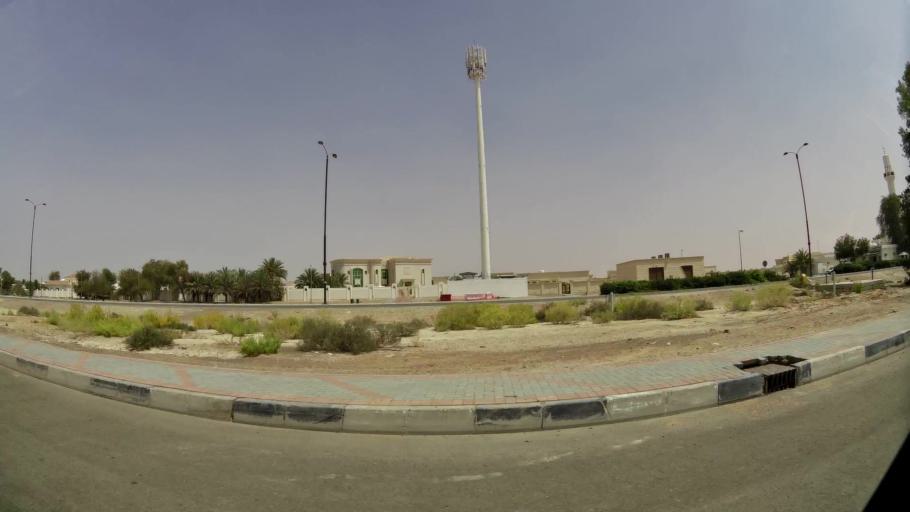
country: AE
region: Abu Dhabi
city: Al Ain
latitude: 24.1408
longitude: 55.6414
